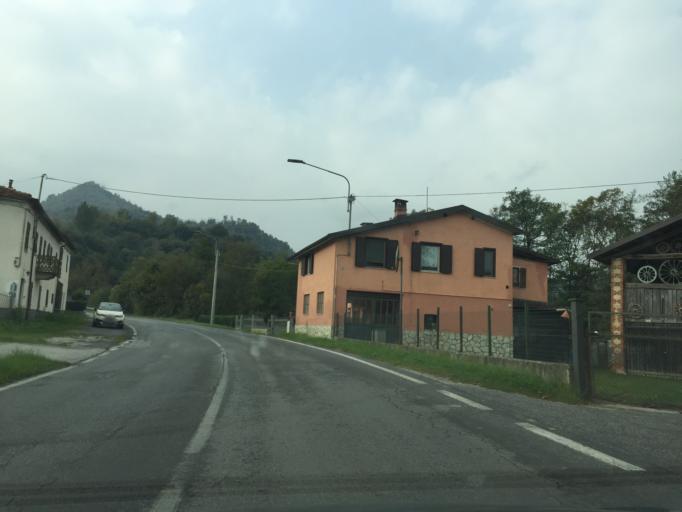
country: IT
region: Piedmont
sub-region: Provincia di Cuneo
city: Roccaforte Mondovi
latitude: 44.3126
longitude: 7.7235
